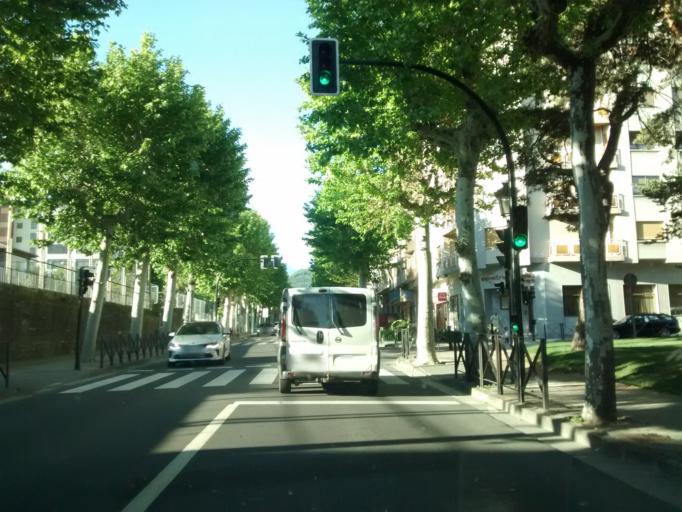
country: ES
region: Aragon
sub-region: Provincia de Huesca
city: Jaca
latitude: 42.5676
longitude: -0.5532
